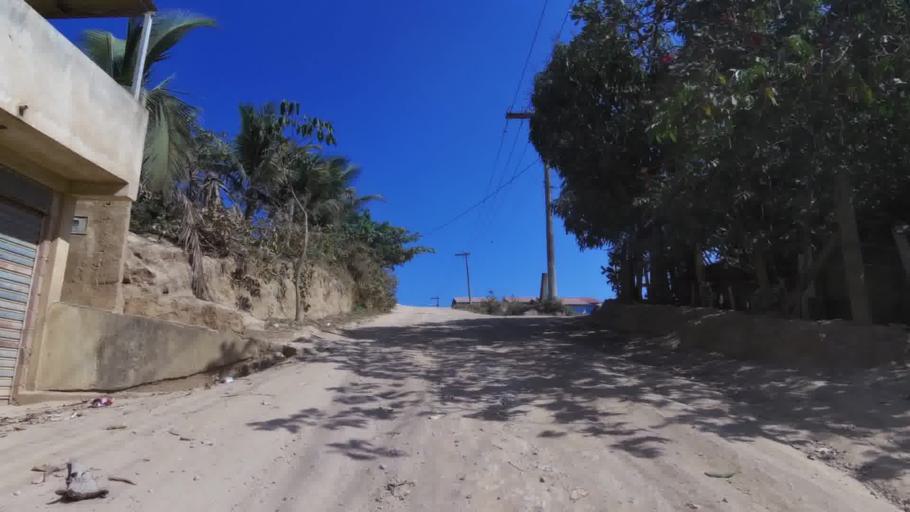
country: BR
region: Espirito Santo
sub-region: Marataizes
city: Marataizes
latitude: -21.0311
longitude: -40.8226
